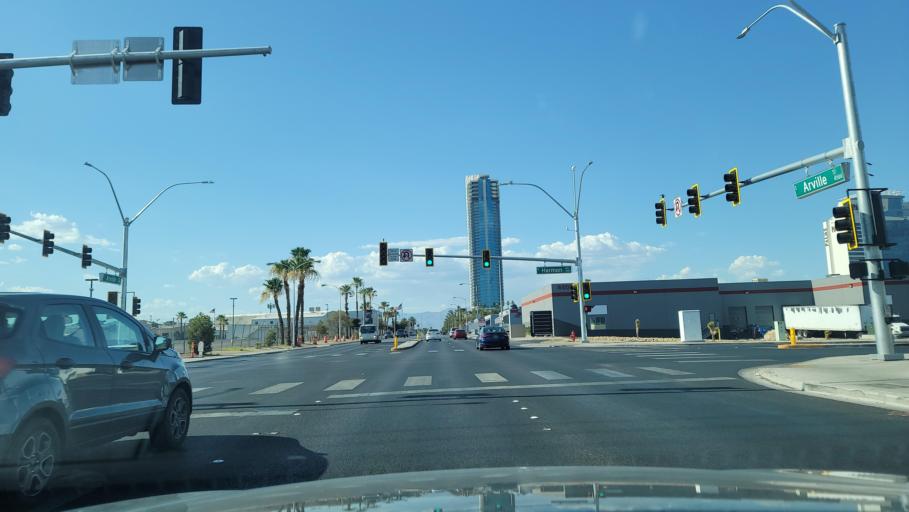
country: US
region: Nevada
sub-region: Clark County
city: Spring Valley
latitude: 36.1080
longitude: -115.1993
